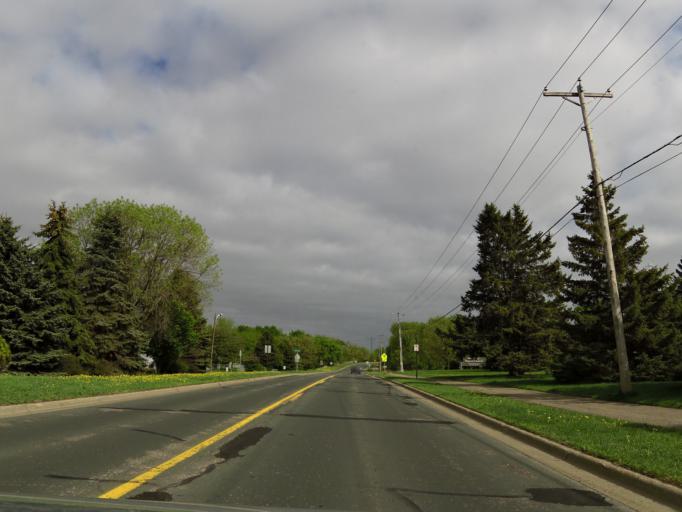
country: US
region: Minnesota
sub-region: Washington County
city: Woodbury
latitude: 44.9311
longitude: -92.9712
